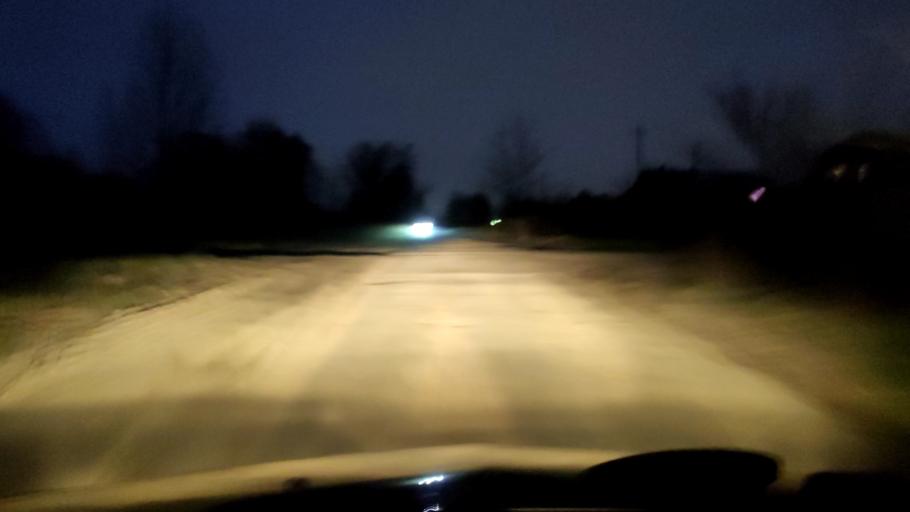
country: RU
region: Voronezj
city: Pridonskoy
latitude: 51.6369
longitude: 39.0894
